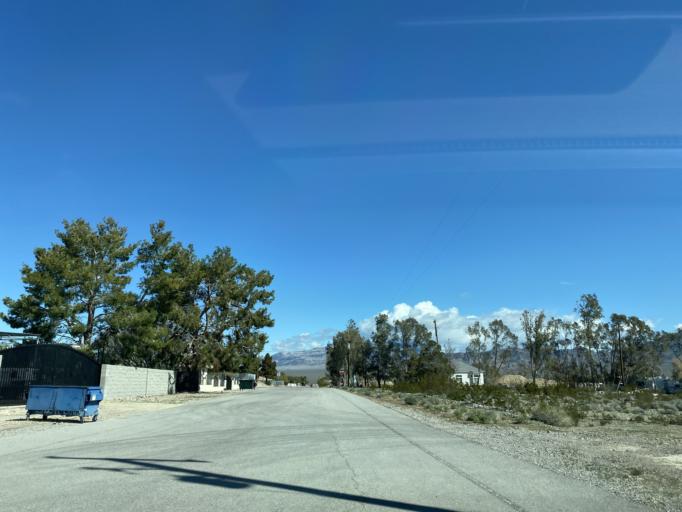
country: US
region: Nevada
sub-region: Clark County
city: North Las Vegas
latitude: 36.3257
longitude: -115.2852
